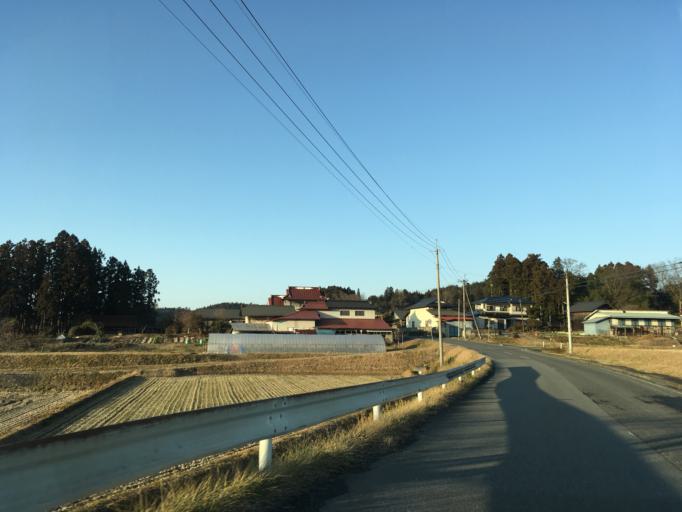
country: JP
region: Iwate
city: Ichinoseki
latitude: 38.8162
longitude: 141.2141
